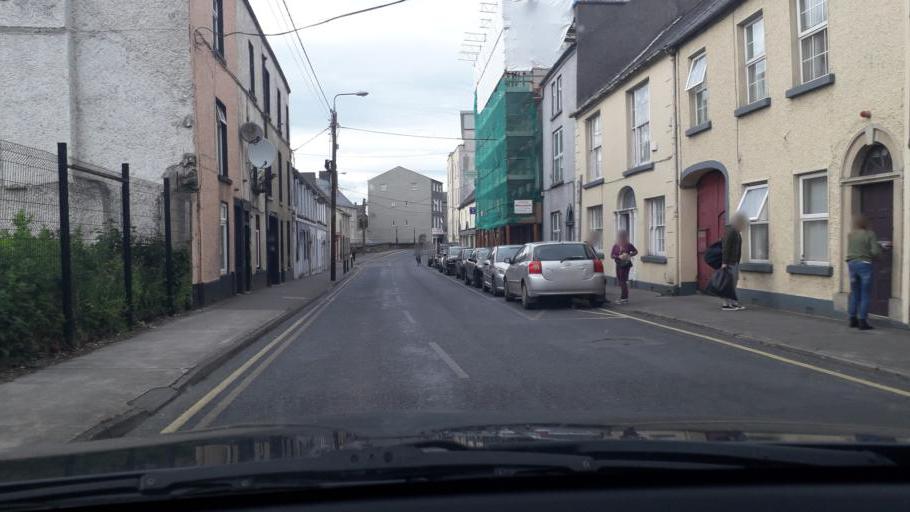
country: IE
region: Leinster
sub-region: County Carlow
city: Carlow
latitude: 52.8346
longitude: -6.9328
